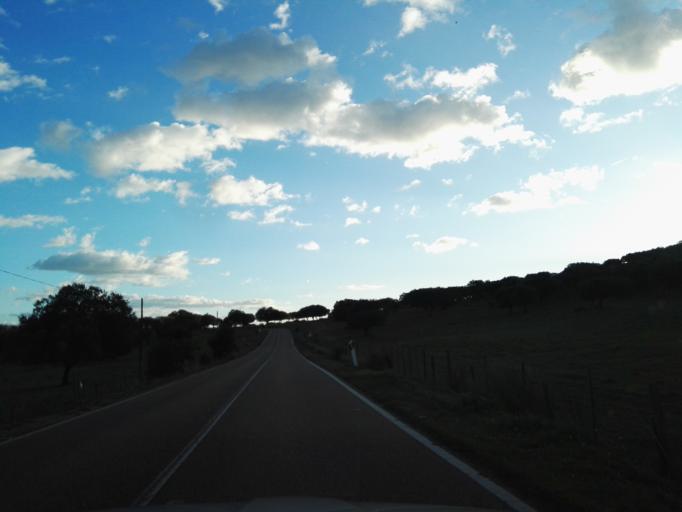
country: PT
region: Portalegre
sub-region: Elvas
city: Elvas
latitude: 38.8216
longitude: -7.1664
